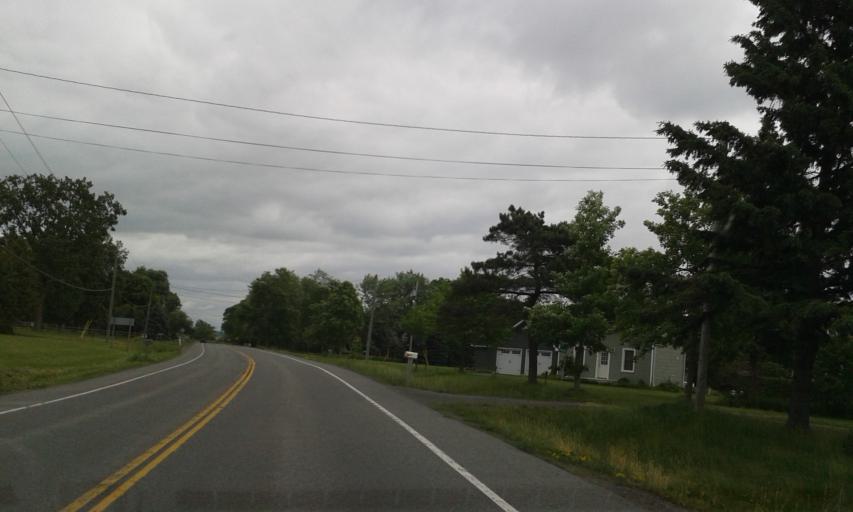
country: CA
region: Ontario
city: Skatepark
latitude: 44.1284
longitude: -76.8800
